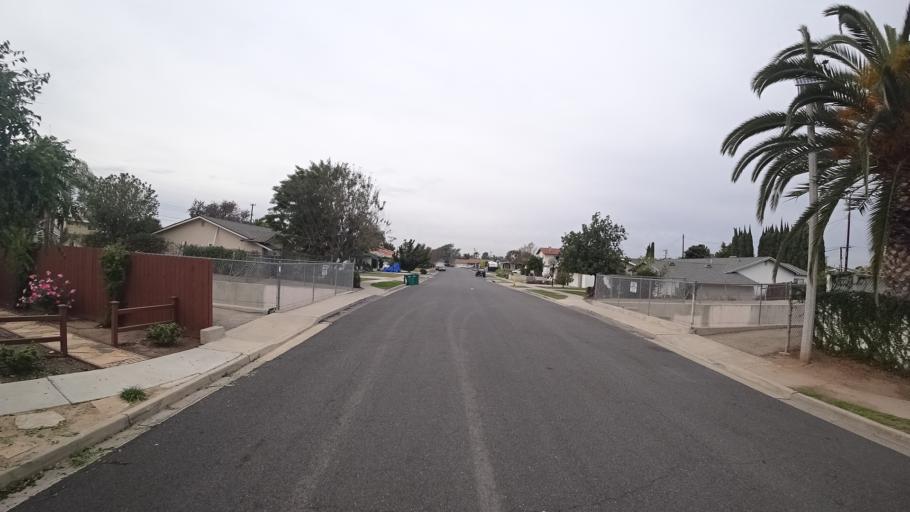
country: US
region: California
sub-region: Orange County
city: Tustin
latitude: 33.7387
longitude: -117.8017
